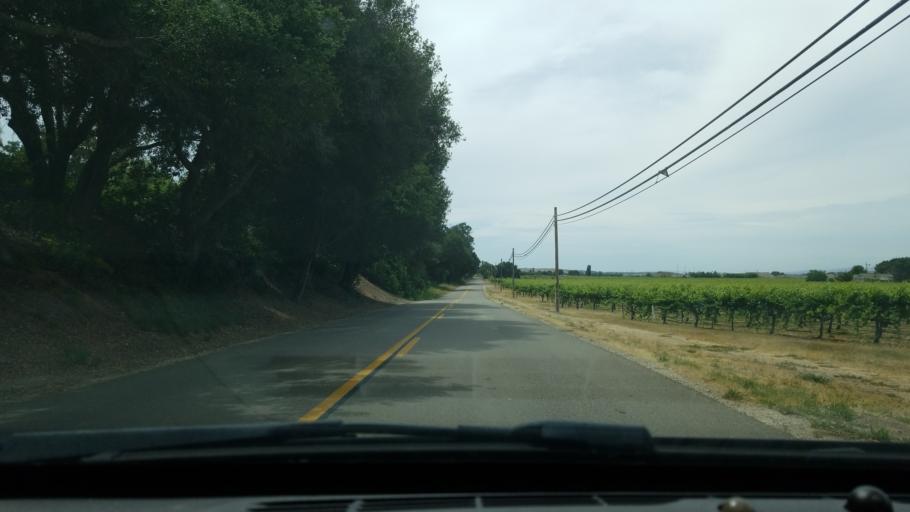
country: US
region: California
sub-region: Santa Barbara County
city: Los Alamos
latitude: 34.8552
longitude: -120.2662
